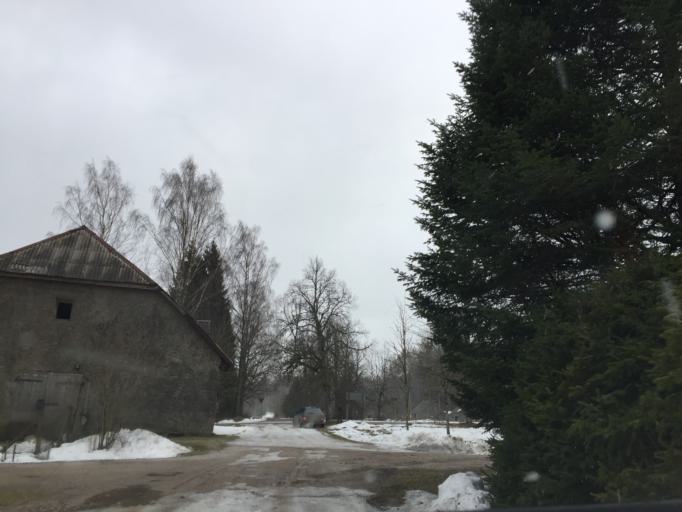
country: LV
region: Salacgrivas
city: Salacgriva
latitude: 57.6509
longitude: 24.4911
